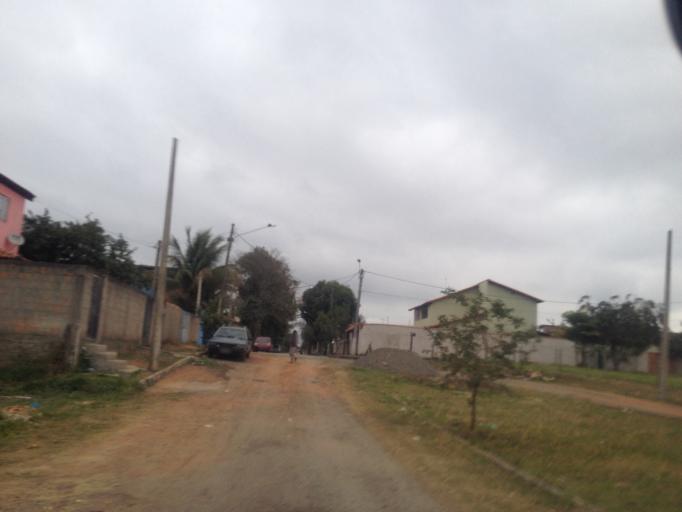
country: BR
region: Rio de Janeiro
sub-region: Porto Real
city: Porto Real
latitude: -22.4072
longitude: -44.2979
